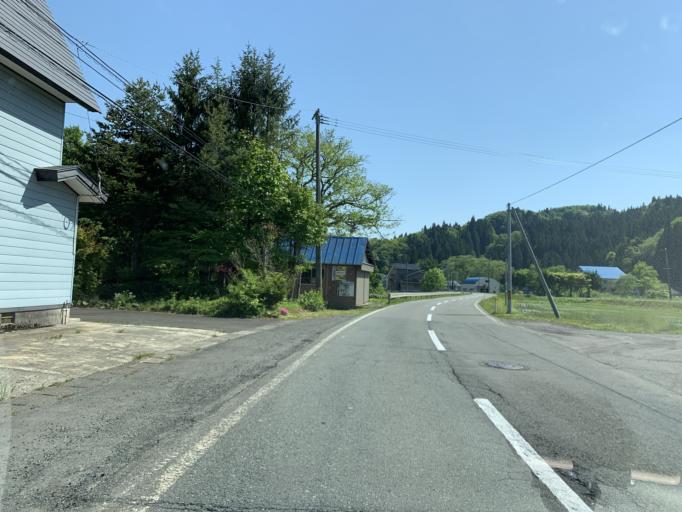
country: JP
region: Iwate
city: Shizukuishi
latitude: 39.5137
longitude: 140.8290
